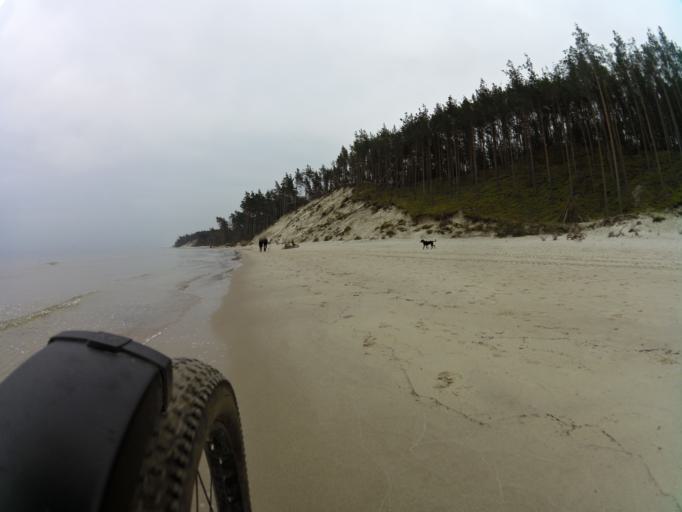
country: PL
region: Pomeranian Voivodeship
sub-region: Powiat pucki
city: Krokowa
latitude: 54.8314
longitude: 18.1341
